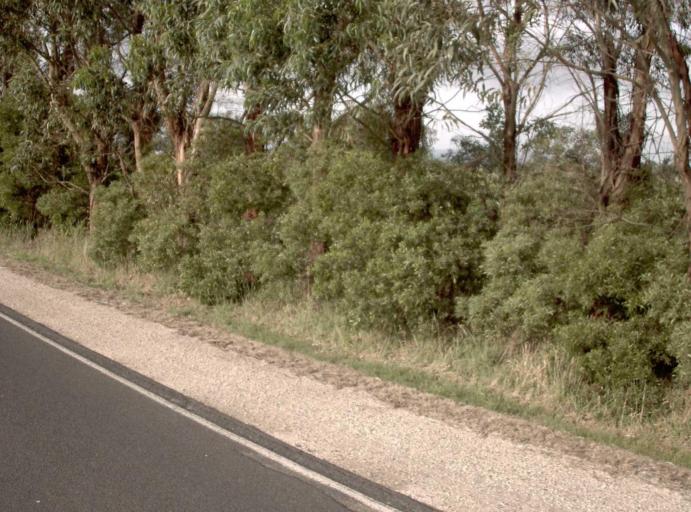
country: AU
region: Victoria
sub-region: Wellington
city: Sale
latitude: -37.9093
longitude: 146.9956
